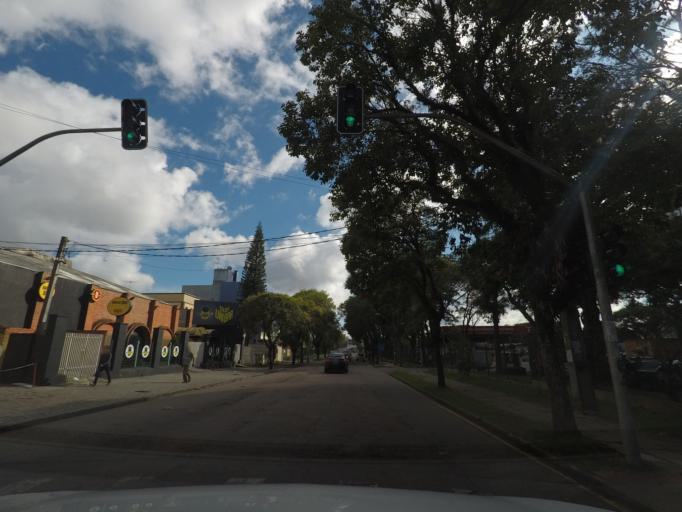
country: BR
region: Parana
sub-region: Curitiba
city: Curitiba
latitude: -25.4500
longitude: -49.2530
